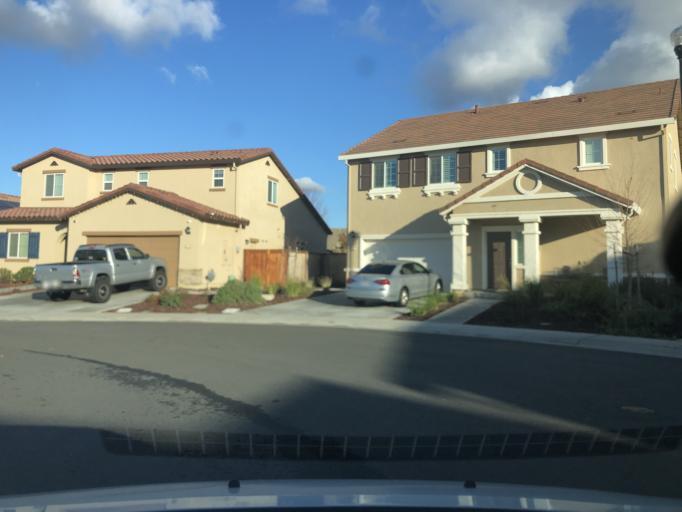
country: US
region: California
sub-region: Sacramento County
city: Antelope
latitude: 38.7725
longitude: -121.3777
